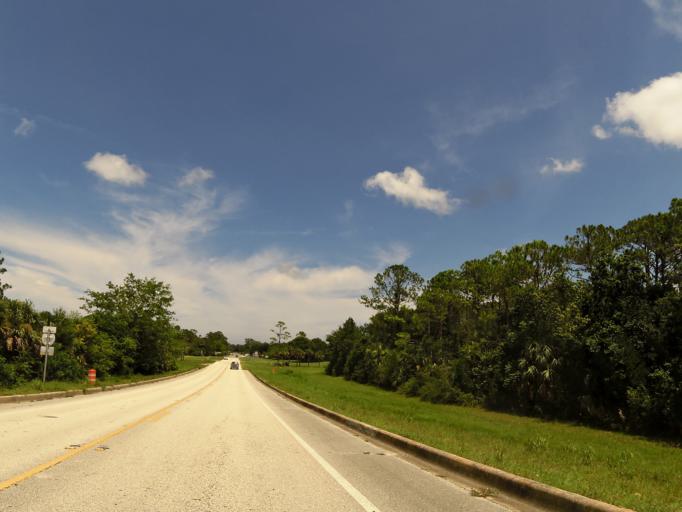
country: US
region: Florida
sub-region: Flagler County
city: Flagler Beach
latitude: 29.4037
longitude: -81.1538
